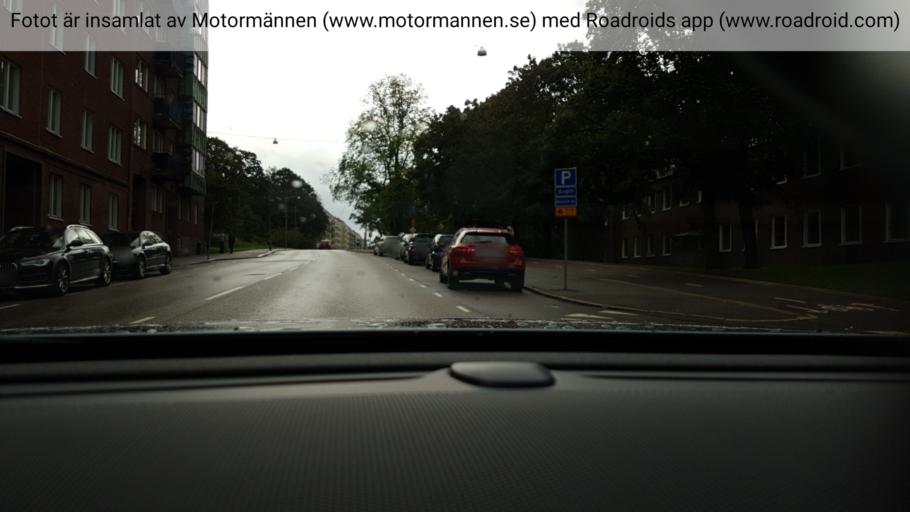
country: SE
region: Vaestra Goetaland
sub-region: Goteborg
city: Goeteborg
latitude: 57.6919
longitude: 11.9780
